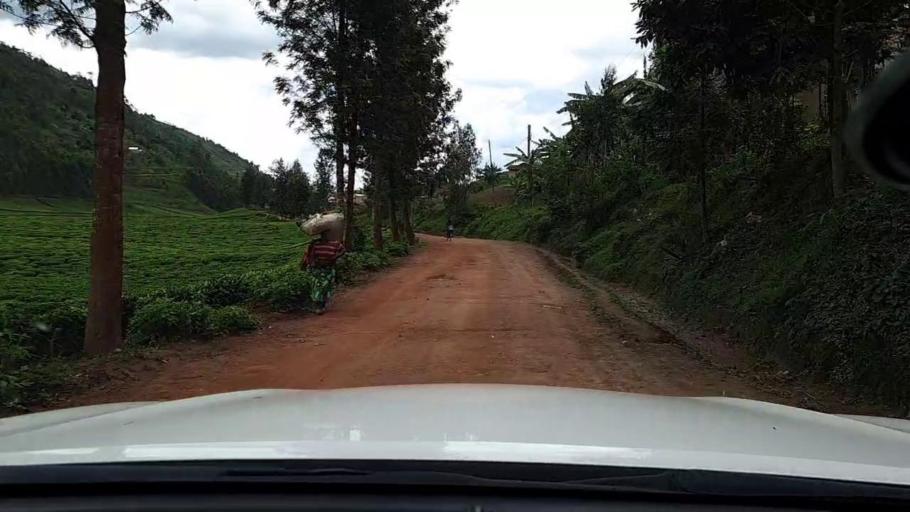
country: RW
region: Northern Province
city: Byumba
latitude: -1.6567
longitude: 29.9092
